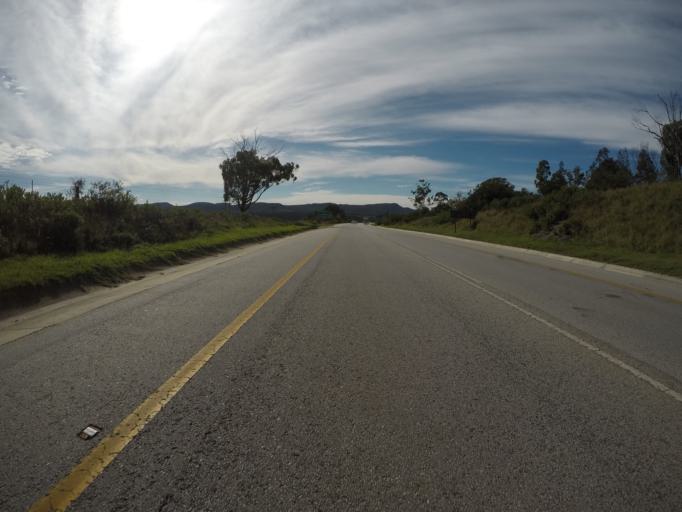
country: ZA
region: Eastern Cape
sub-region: Cacadu District Municipality
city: Jeffrey's Bay
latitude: -33.8929
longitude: 25.1327
